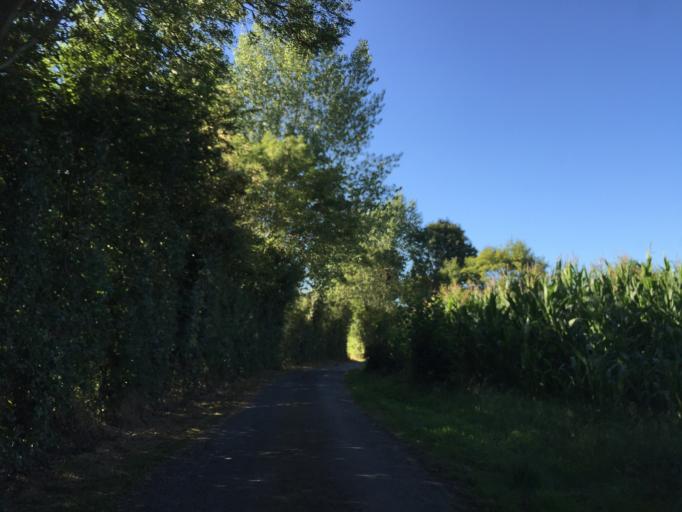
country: FR
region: Lower Normandy
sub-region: Departement du Calvados
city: Equemauville
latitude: 49.4034
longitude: 0.1949
